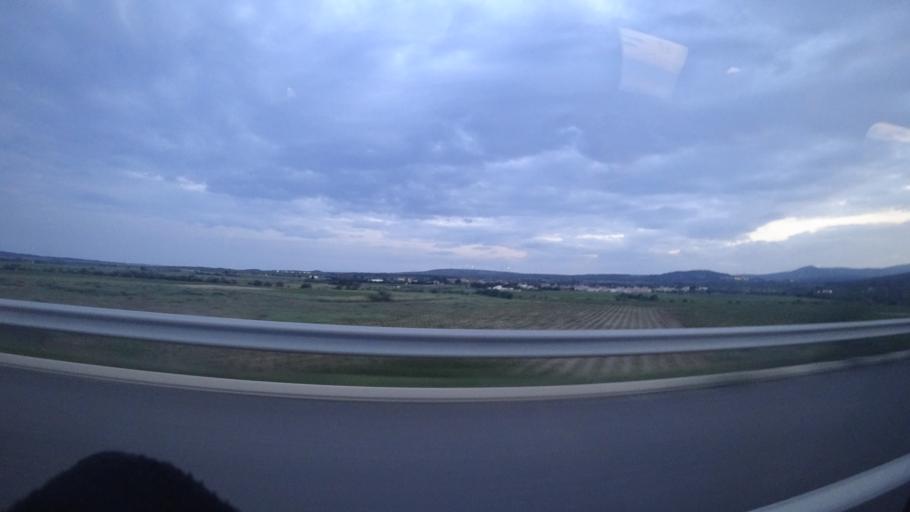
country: FR
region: Languedoc-Roussillon
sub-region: Departement de l'Aude
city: Leucate
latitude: 42.9385
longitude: 2.9802
